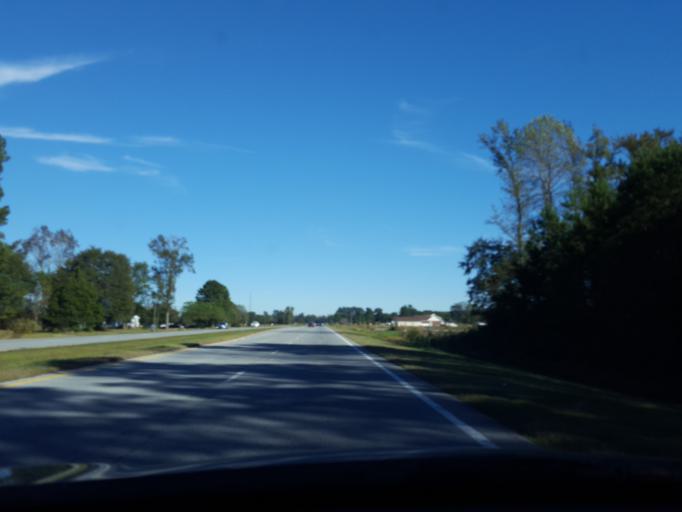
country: US
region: North Carolina
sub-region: Beaufort County
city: Washington
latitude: 35.6262
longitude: -77.1943
